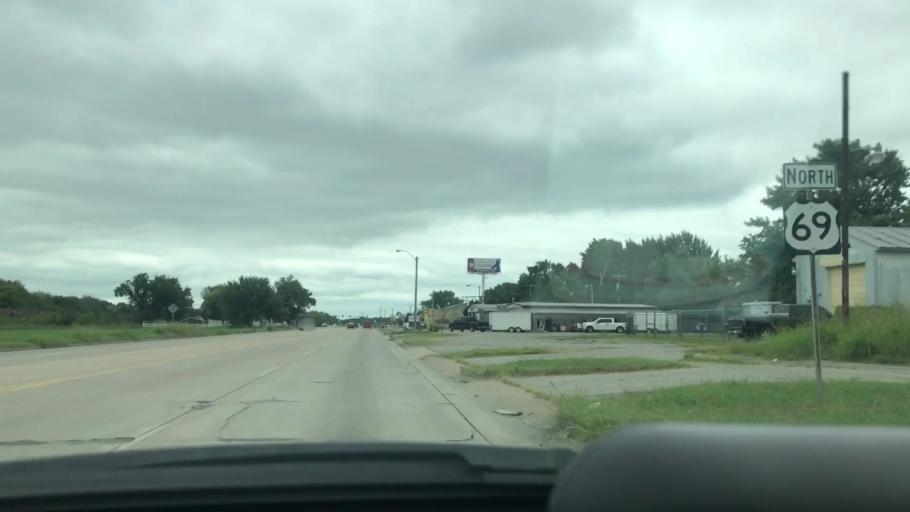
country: US
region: Oklahoma
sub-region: Mayes County
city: Chouteau
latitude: 36.1873
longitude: -95.3425
